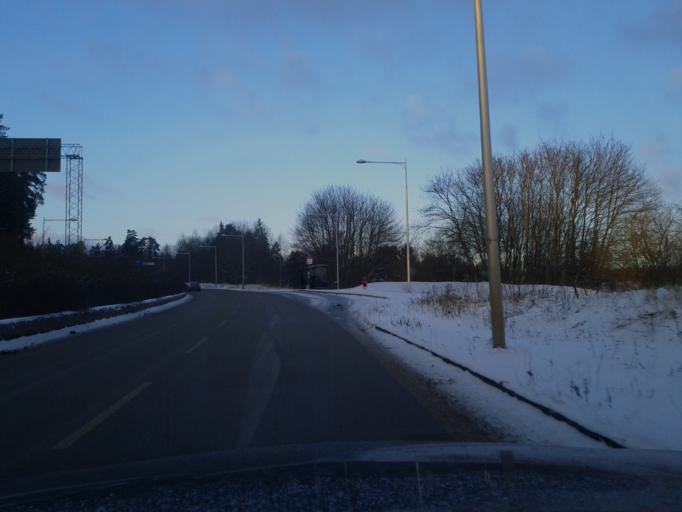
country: SE
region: Stockholm
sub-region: Taby Kommun
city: Taby
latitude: 59.4540
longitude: 18.0866
